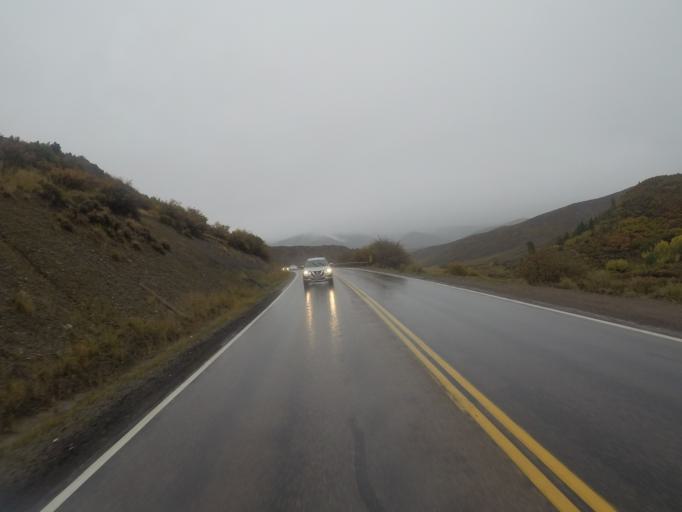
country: US
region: Colorado
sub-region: Pitkin County
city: Snowmass Village
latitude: 39.2321
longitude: -106.9142
